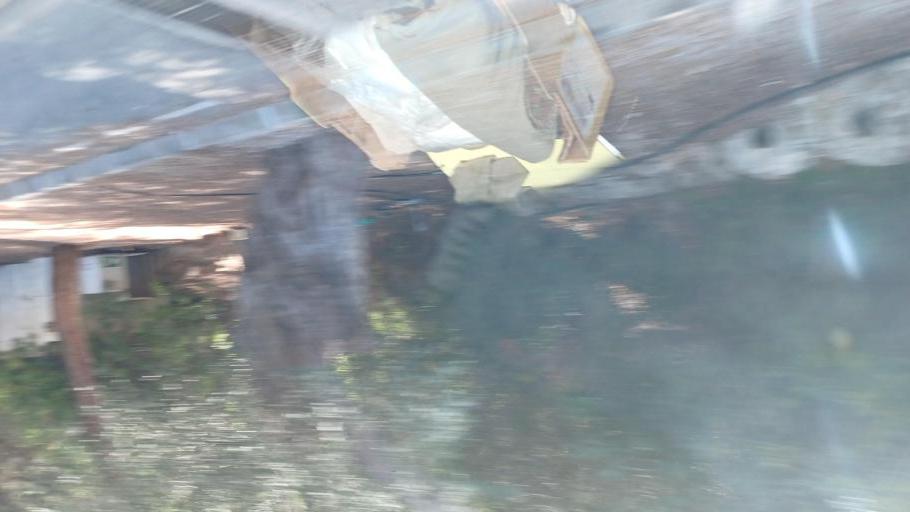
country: CY
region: Pafos
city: Tala
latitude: 34.8452
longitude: 32.4463
